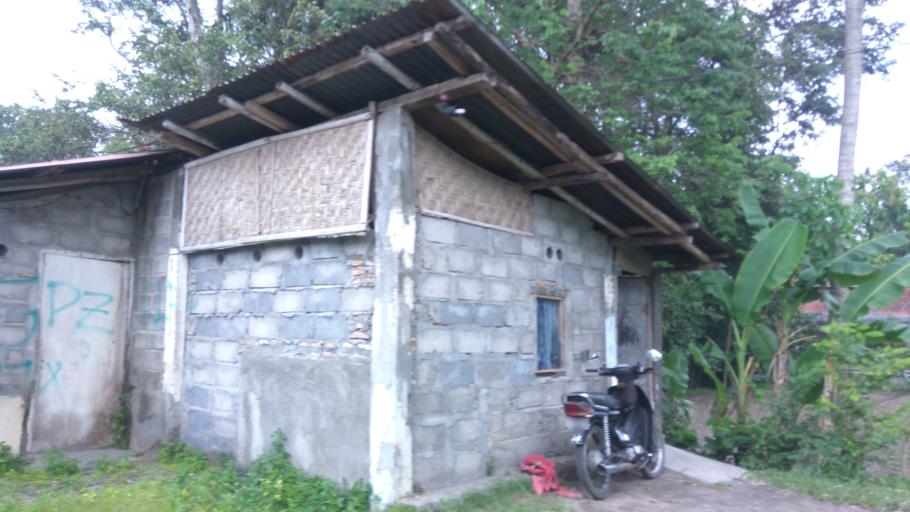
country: ID
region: Daerah Istimewa Yogyakarta
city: Depok
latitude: -7.7377
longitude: 110.4094
